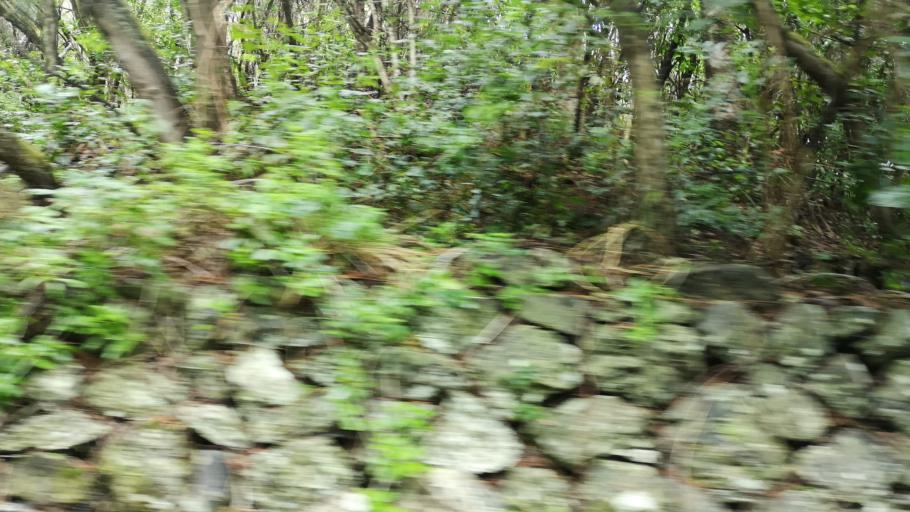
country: ES
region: Canary Islands
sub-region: Provincia de Santa Cruz de Tenerife
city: Vallehermosa
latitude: 28.1612
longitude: -17.2925
